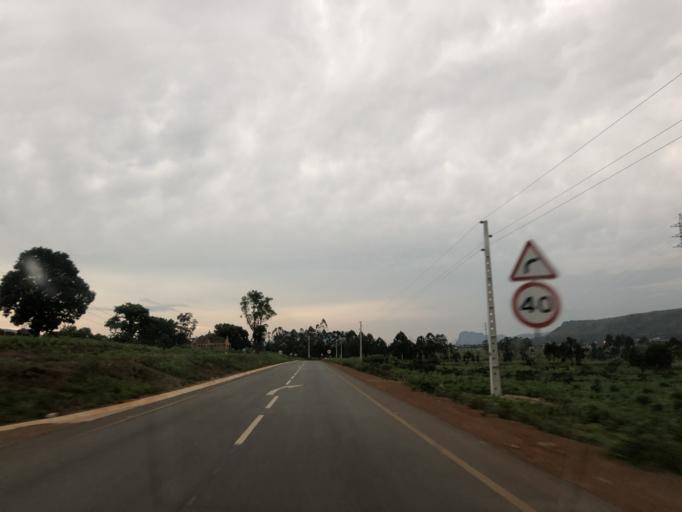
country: AO
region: Cuanza Sul
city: Uacu Cungo
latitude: -11.3326
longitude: 15.0997
